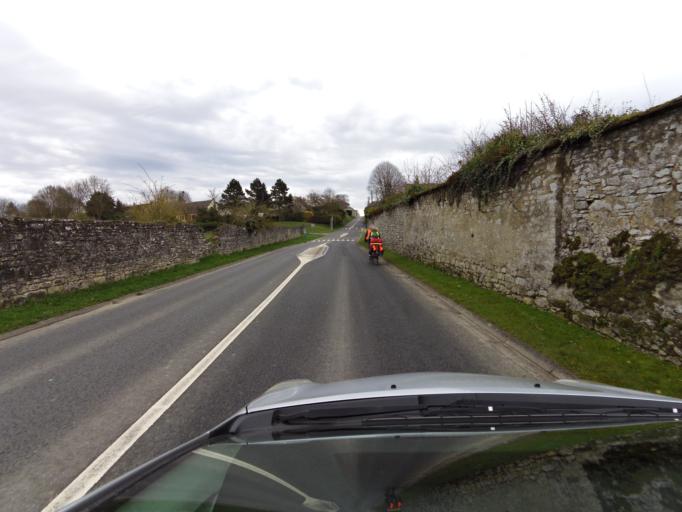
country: FR
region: Picardie
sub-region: Departement de l'Oise
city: Chamant
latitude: 49.1962
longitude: 2.6261
